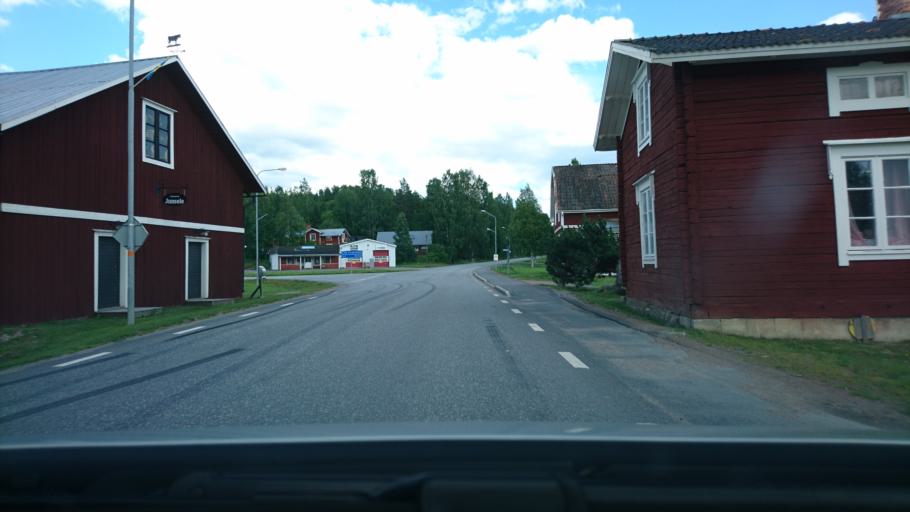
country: SE
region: Vaesternorrland
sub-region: Solleftea Kommun
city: As
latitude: 63.6948
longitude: 16.8883
